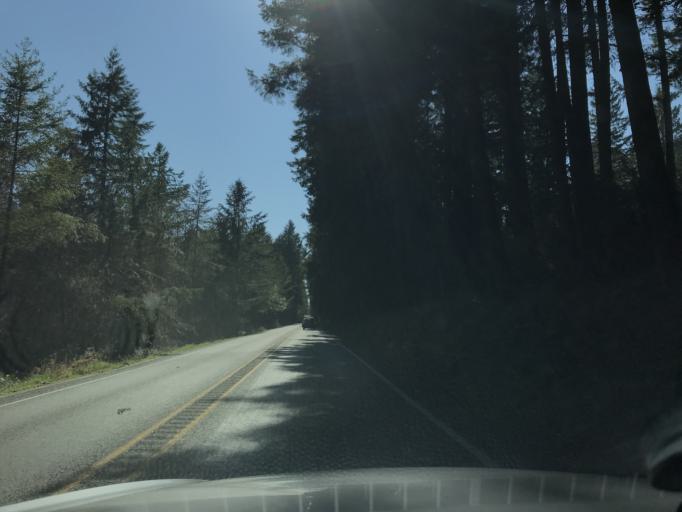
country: US
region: Washington
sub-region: Pierce County
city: Key Center
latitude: 47.3580
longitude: -122.7312
